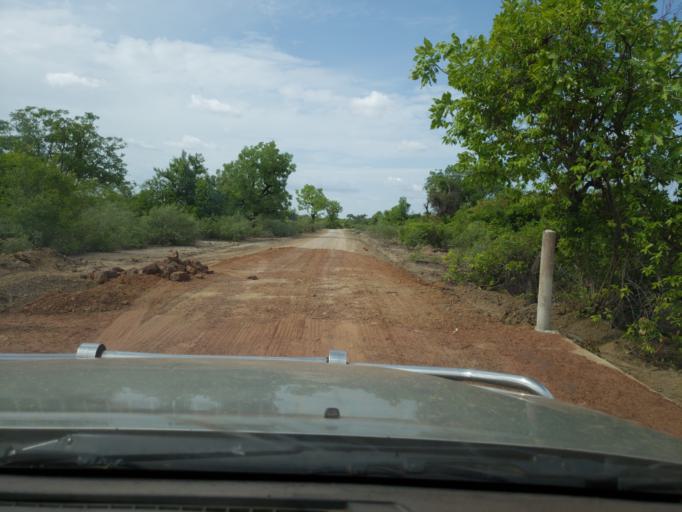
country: ML
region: Segou
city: Bla
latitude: 12.7653
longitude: -5.6213
